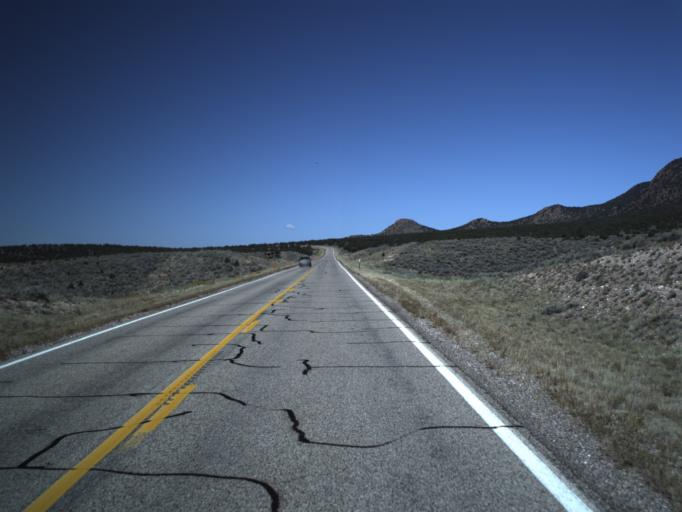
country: US
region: Utah
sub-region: Washington County
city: Enterprise
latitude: 37.6534
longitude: -113.4527
